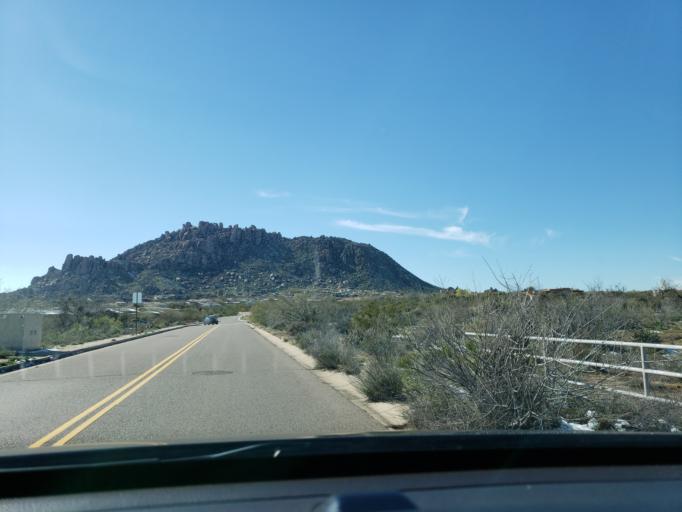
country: US
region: Arizona
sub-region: Maricopa County
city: Carefree
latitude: 33.7162
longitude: -111.8251
